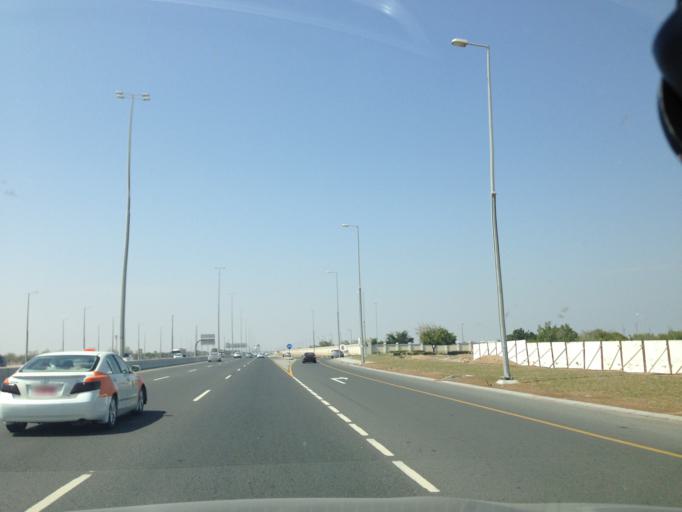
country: OM
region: Muhafazat Masqat
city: As Sib al Jadidah
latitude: 23.6602
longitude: 58.1832
